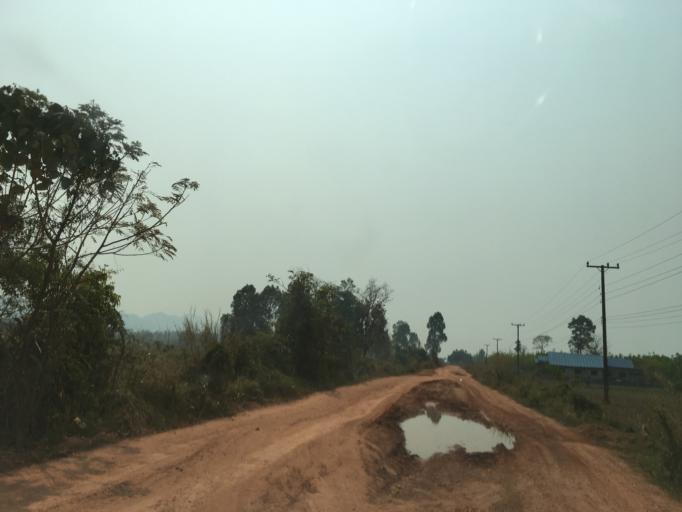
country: TH
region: Changwat Bueng Kan
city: Bung Khla
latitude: 18.2091
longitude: 104.0735
